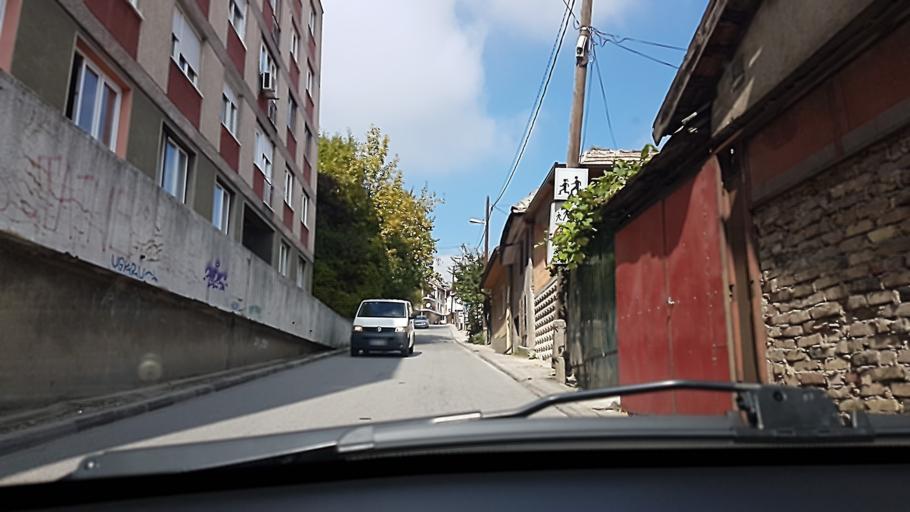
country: BA
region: Federation of Bosnia and Herzegovina
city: Kobilja Glava
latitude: 43.8603
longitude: 18.4092
